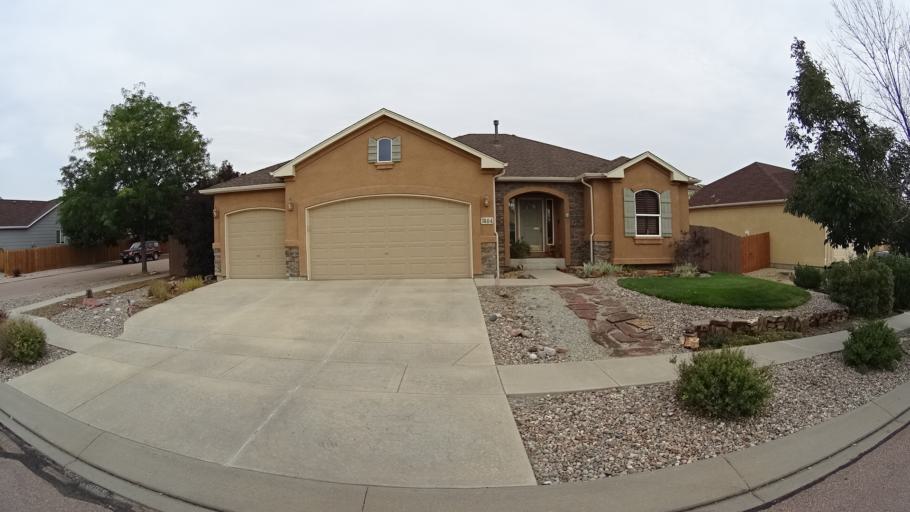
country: US
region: Colorado
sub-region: El Paso County
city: Cimarron Hills
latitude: 38.9142
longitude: -104.6896
